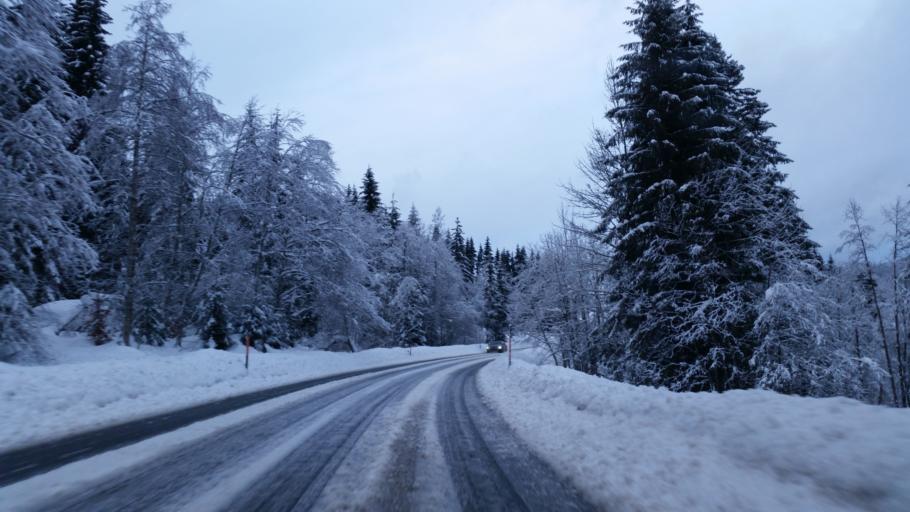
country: AT
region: Tyrol
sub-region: Politischer Bezirk Kitzbuhel
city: Hochfilzen
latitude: 47.4551
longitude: 12.6450
